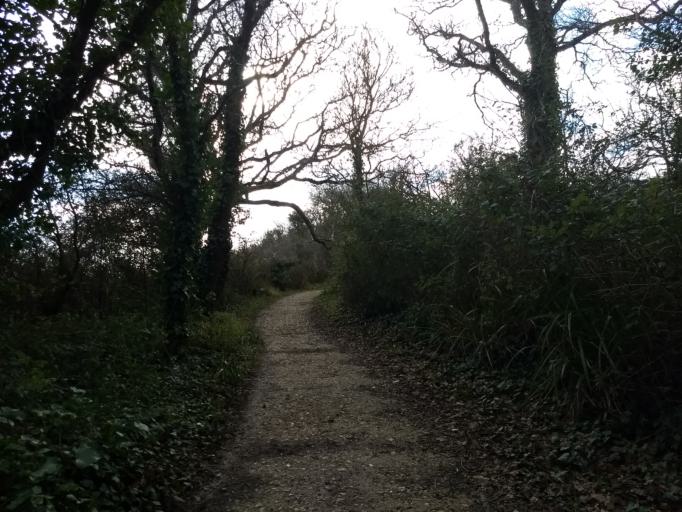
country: GB
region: England
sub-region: Isle of Wight
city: Bembridge
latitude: 50.6765
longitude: -1.0873
